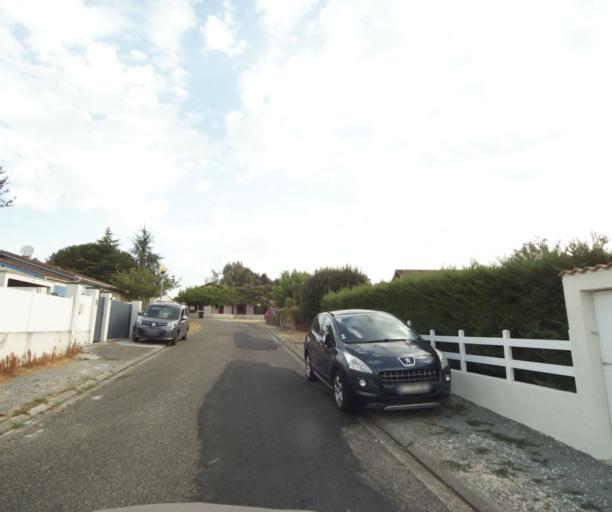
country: FR
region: Aquitaine
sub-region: Departement de la Gironde
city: Creon
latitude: 44.7680
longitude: -0.3544
